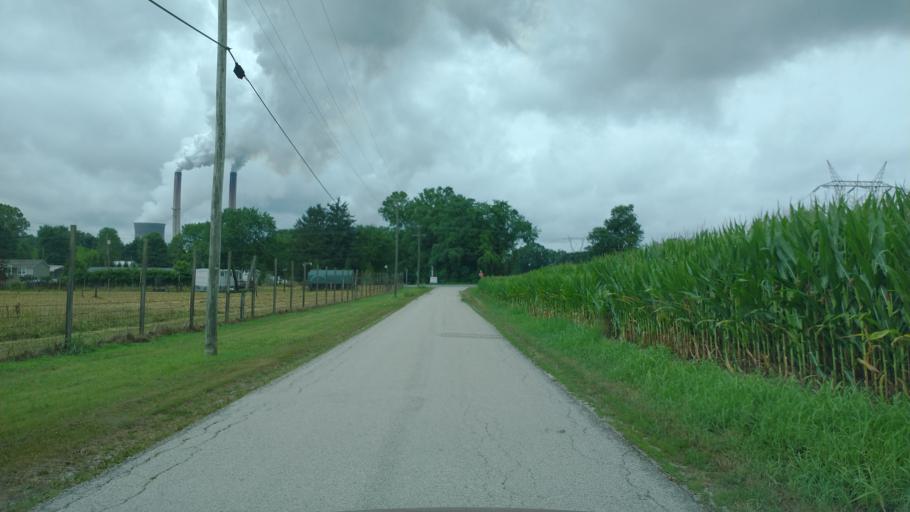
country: US
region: Ohio
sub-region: Meigs County
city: Middleport
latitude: 38.9364
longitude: -82.0945
